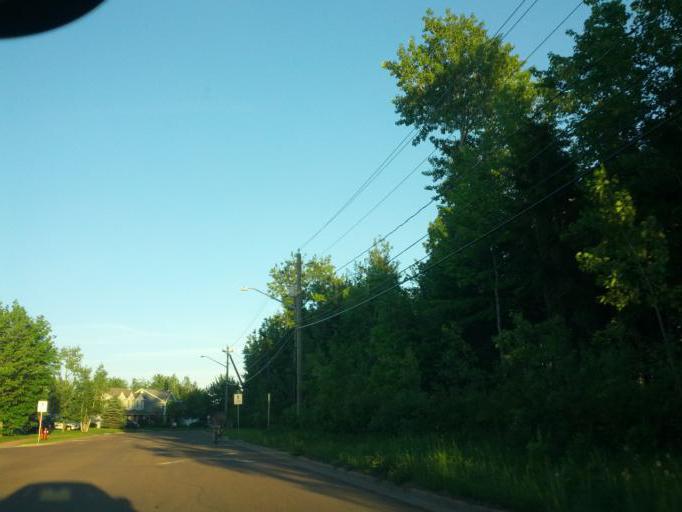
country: CA
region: New Brunswick
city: Moncton
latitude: 46.1166
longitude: -64.8695
